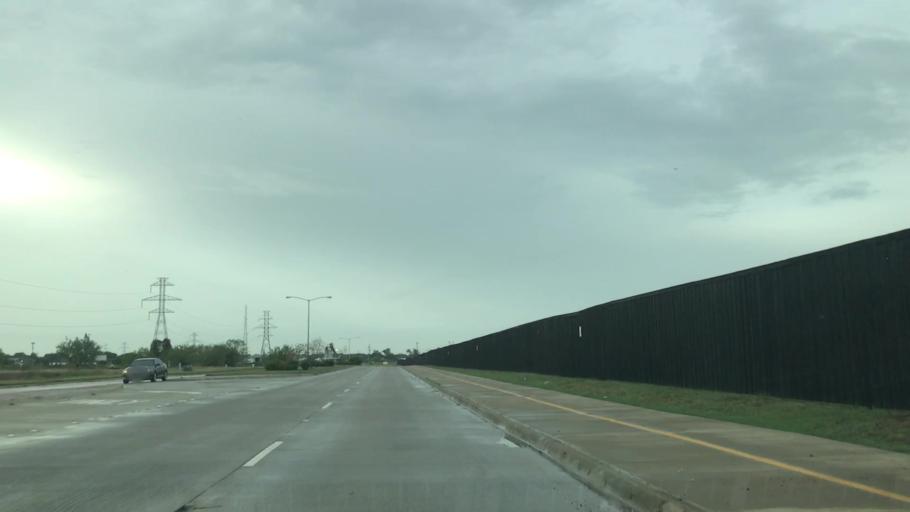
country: US
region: Texas
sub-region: Denton County
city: Lewisville
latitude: 33.0458
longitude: -96.9776
